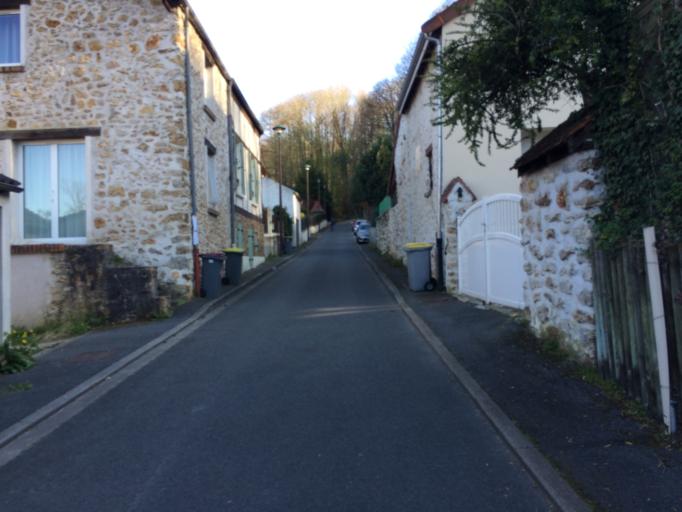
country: FR
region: Ile-de-France
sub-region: Departement de l'Essonne
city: Villejust
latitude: 48.6955
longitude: 2.2246
